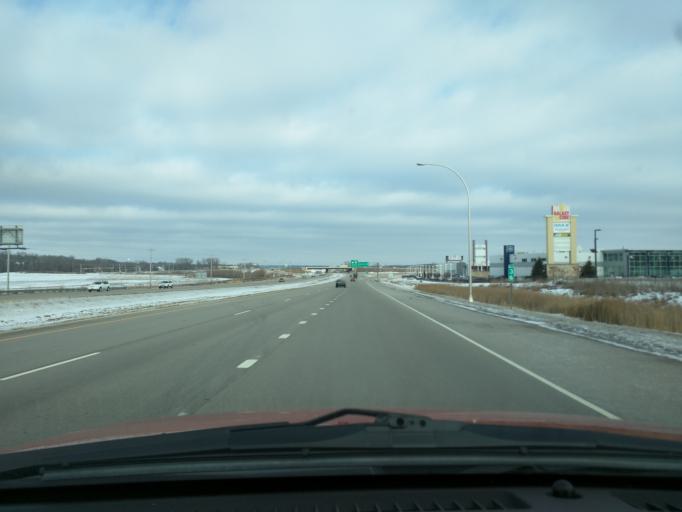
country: US
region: Minnesota
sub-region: Olmsted County
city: Rochester
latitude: 43.9564
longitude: -92.4665
